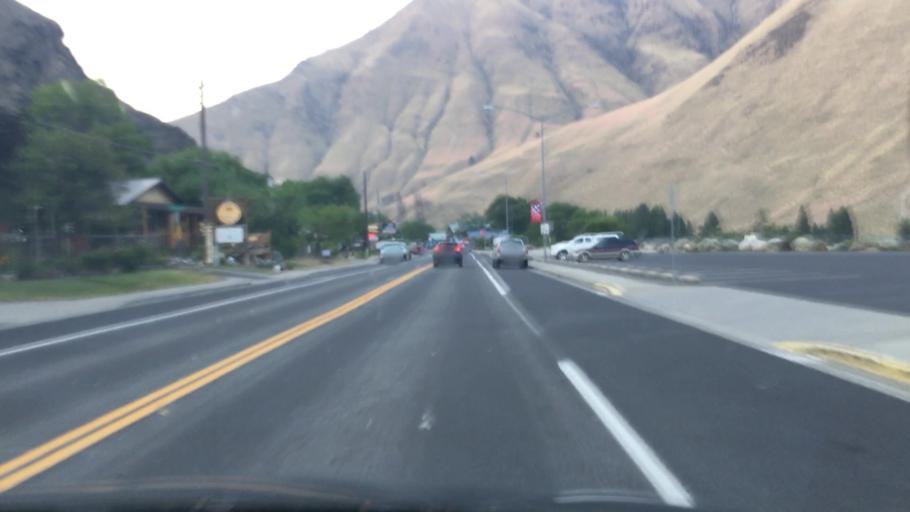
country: US
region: Idaho
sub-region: Idaho County
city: Grangeville
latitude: 45.4246
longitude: -116.3131
